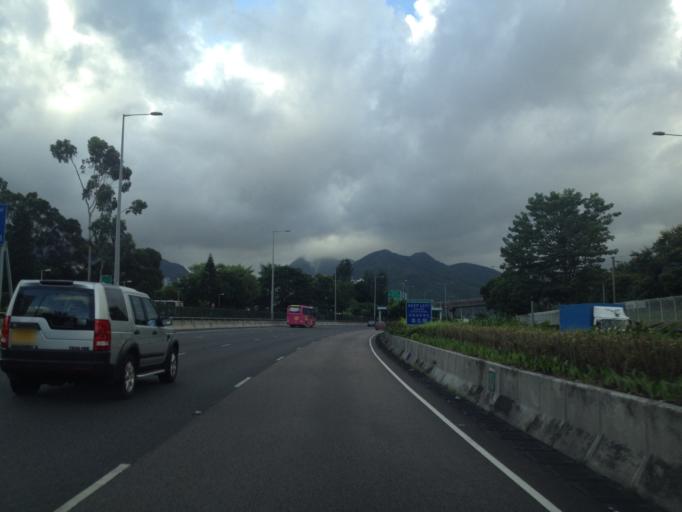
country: HK
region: Sha Tin
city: Sha Tin
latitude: 22.4224
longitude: 114.2129
